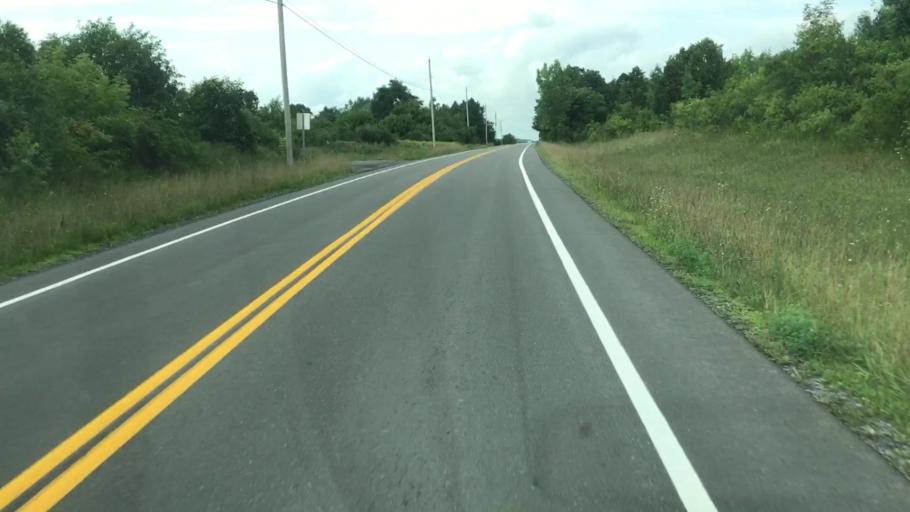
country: US
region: New York
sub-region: Onondaga County
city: Elbridge
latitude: 42.9985
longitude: -76.4399
